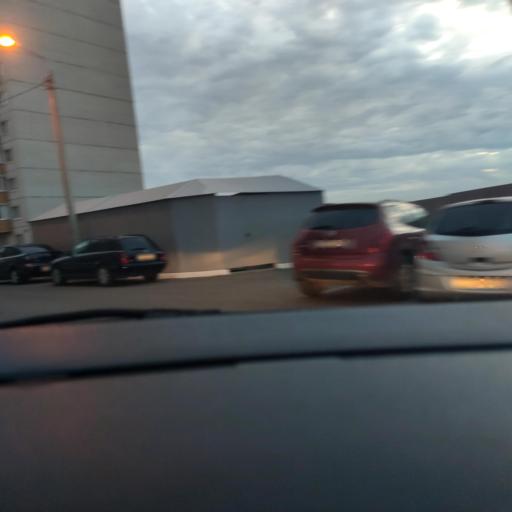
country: RU
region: Voronezj
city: Podgornoye
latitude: 51.7210
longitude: 39.1398
